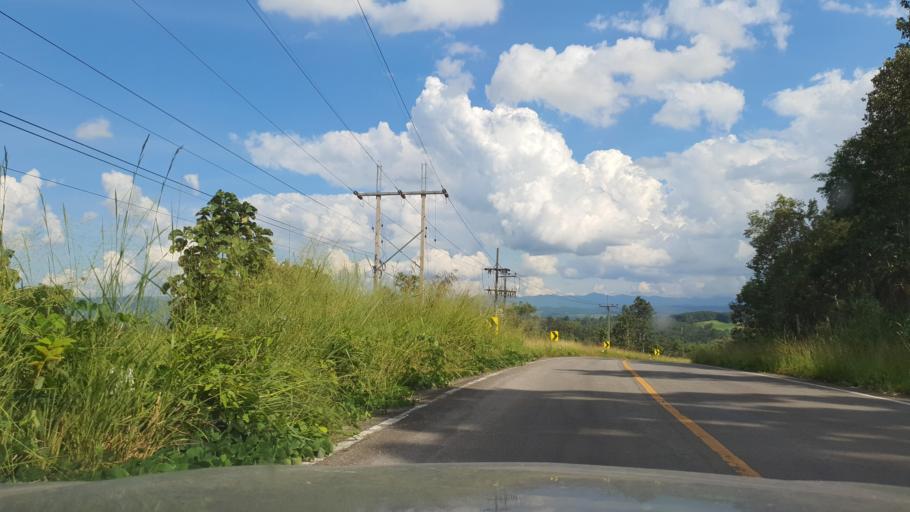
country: TH
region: Chiang Rai
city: Wiang Pa Pao
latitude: 19.3311
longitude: 99.4648
